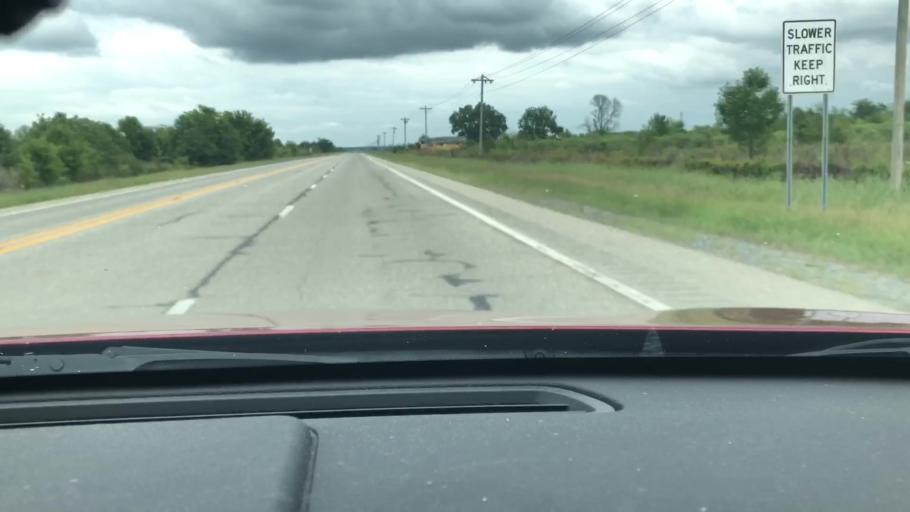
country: US
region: Arkansas
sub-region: Lafayette County
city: Lewisville
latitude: 33.4127
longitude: -93.7984
